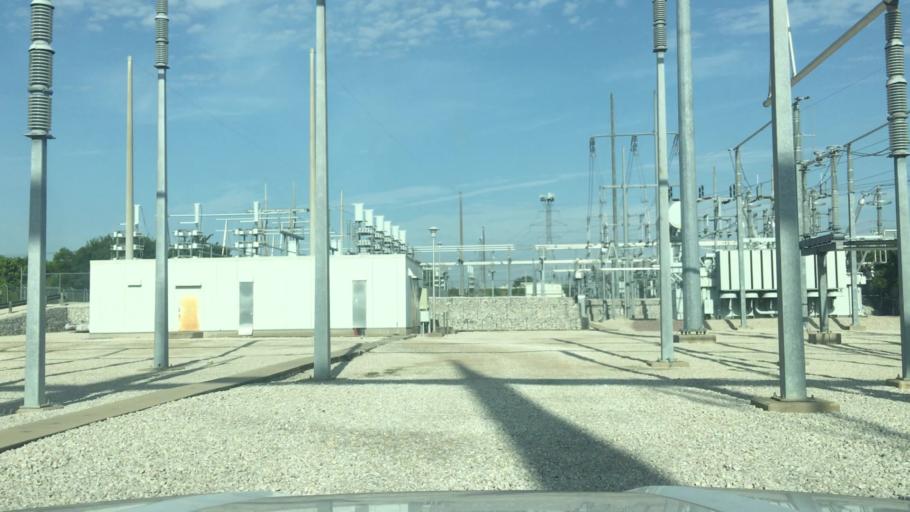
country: US
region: Texas
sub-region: Dallas County
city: Irving
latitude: 32.8152
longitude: -96.9180
